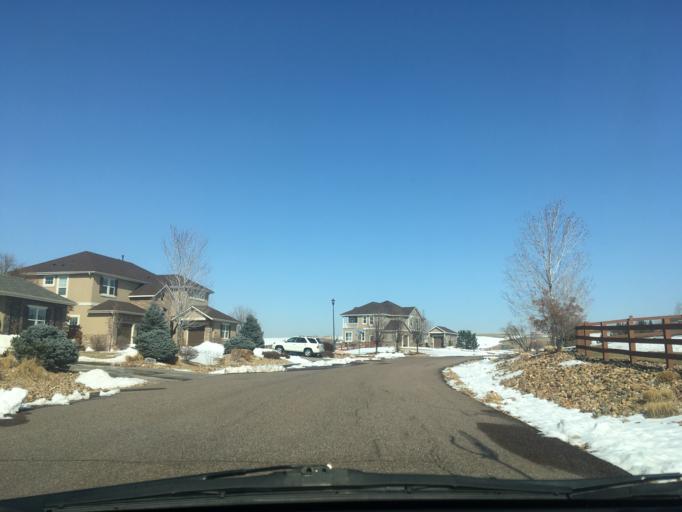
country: US
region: Colorado
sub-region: Boulder County
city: Lafayette
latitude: 39.9718
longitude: -105.0545
